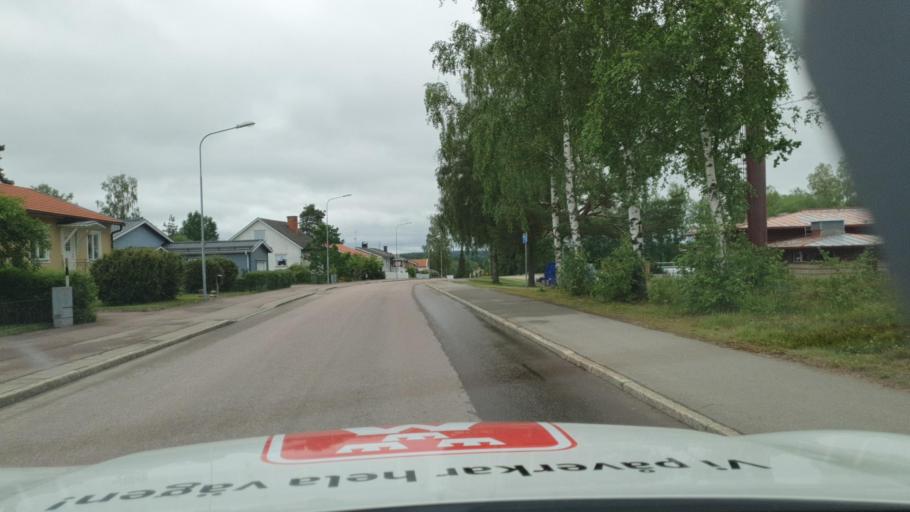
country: SE
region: Vaermland
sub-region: Grums Kommun
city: Grums
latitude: 59.3551
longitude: 13.1050
